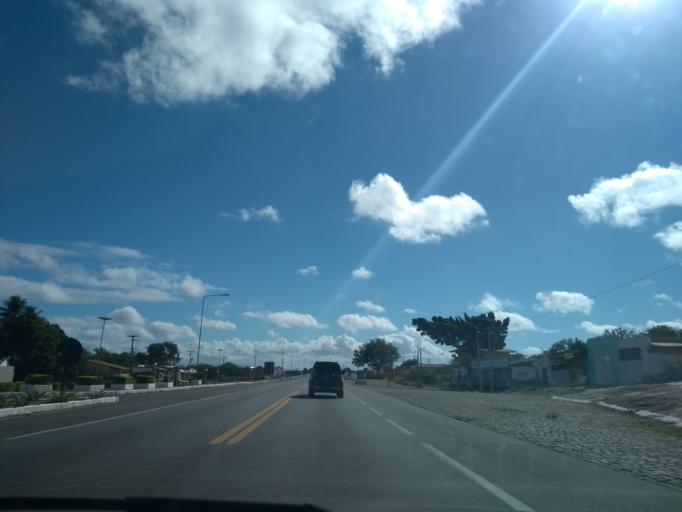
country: BR
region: Bahia
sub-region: Amargosa
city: Amargosa
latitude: -12.8694
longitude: -39.8559
